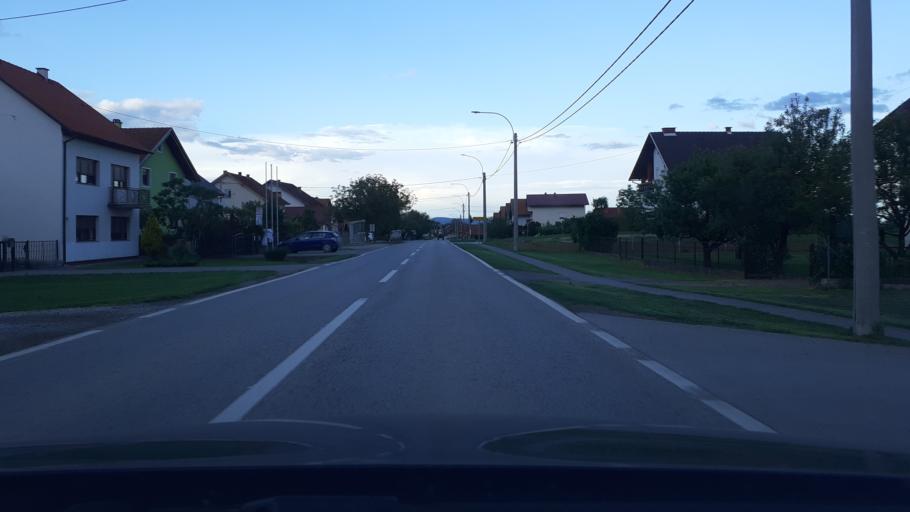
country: HR
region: Pozesko-Slavonska
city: Jaksic
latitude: 45.3583
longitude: 17.7728
